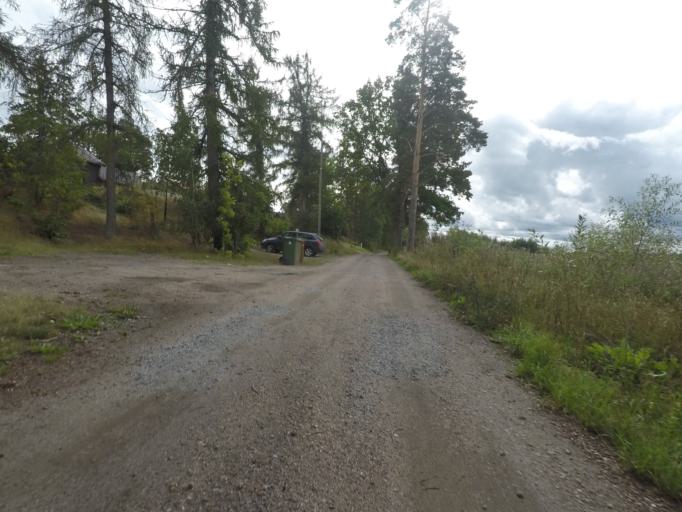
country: SE
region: Vaestmanland
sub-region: Kungsors Kommun
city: Kungsoer
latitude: 59.4643
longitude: 16.0707
